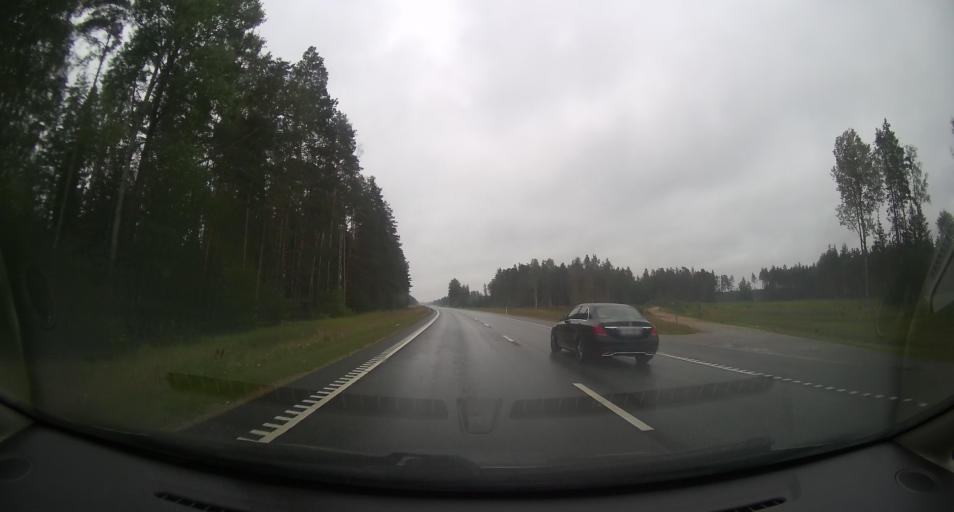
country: EE
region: Harju
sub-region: Loksa linn
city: Loksa
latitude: 59.4567
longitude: 25.8493
